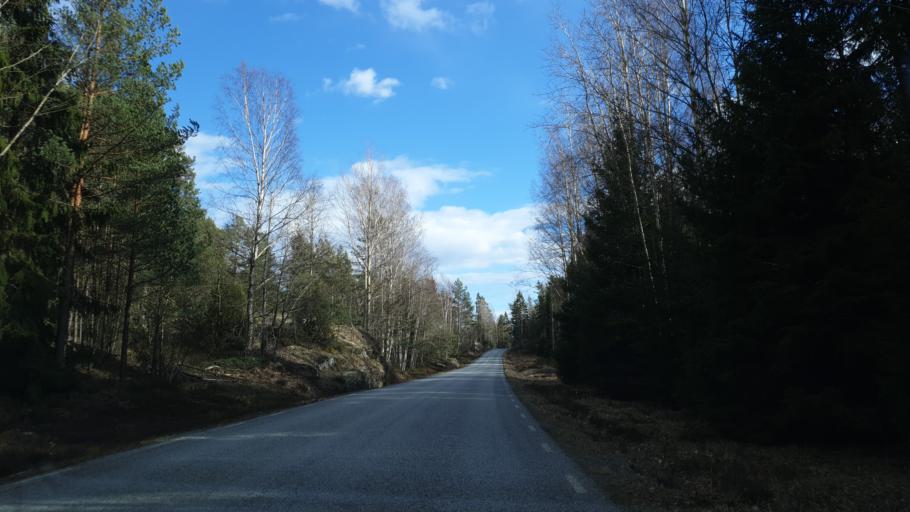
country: SE
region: Stockholm
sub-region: Varmdo Kommun
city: Mortnas
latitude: 59.2448
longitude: 18.4660
